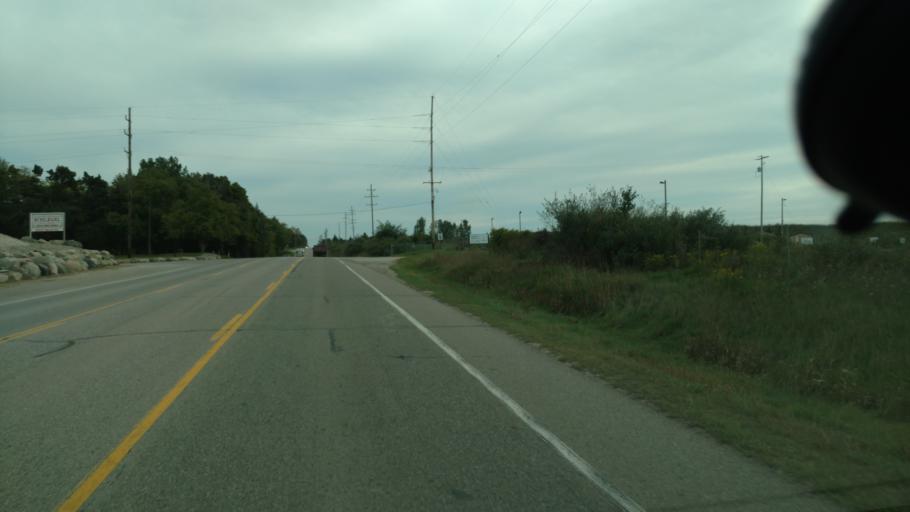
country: US
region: Michigan
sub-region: Ingham County
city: Lansing
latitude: 42.7777
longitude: -84.5231
